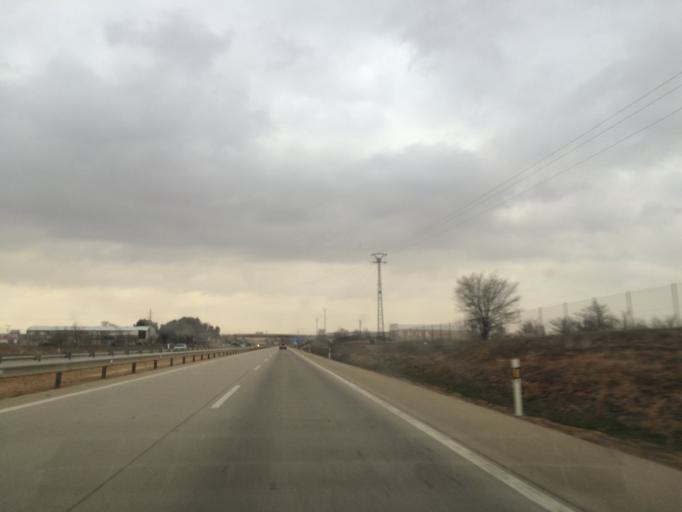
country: ES
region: Castille-La Mancha
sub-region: Province of Toledo
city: Tembleque
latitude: 39.6852
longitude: -3.5028
